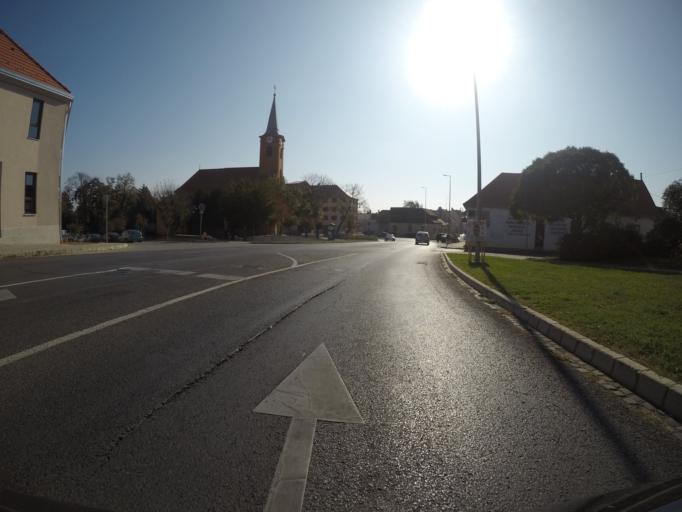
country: HU
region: Baranya
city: Pecs
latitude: 46.0798
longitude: 18.2347
